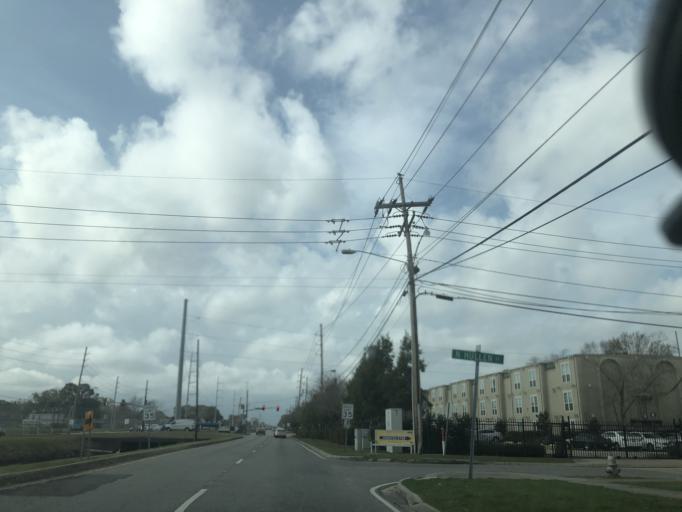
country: US
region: Louisiana
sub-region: Jefferson Parish
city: Metairie
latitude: 29.9925
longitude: -90.1584
